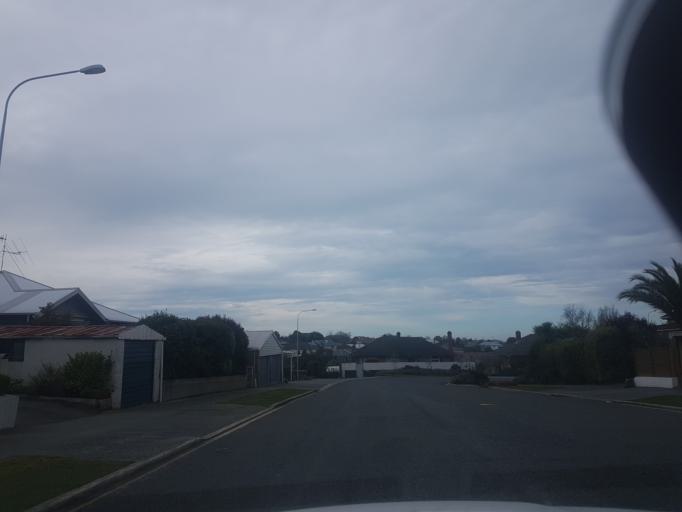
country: NZ
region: Canterbury
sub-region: Timaru District
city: Timaru
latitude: -44.4038
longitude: 171.2334
